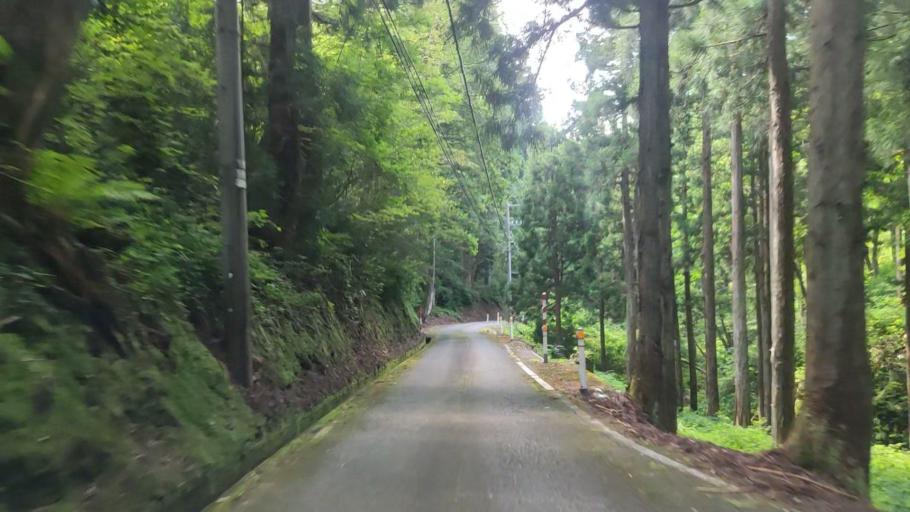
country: JP
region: Ishikawa
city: Komatsu
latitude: 36.2612
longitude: 136.5349
